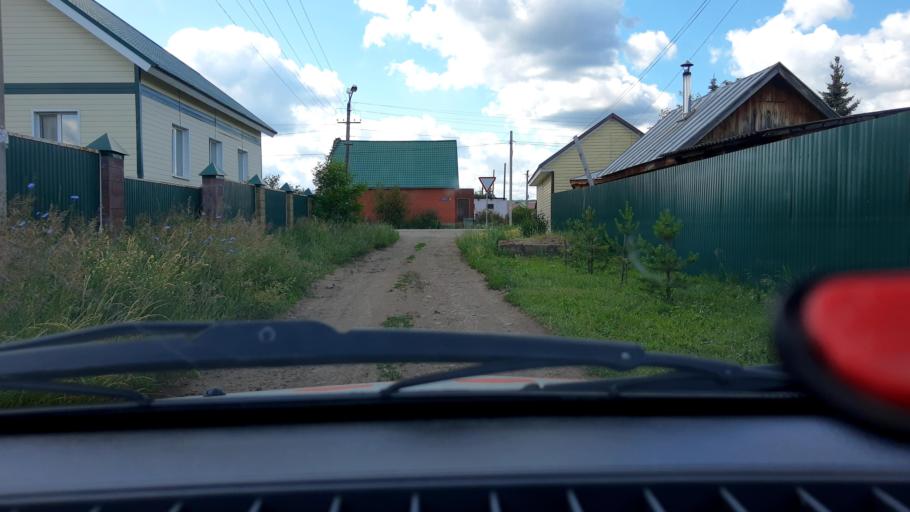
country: RU
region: Bashkortostan
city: Avdon
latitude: 54.4918
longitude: 55.8926
